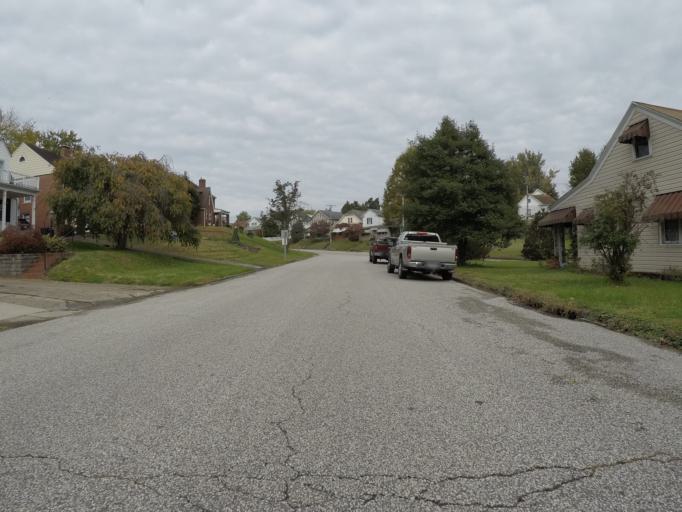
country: US
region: West Virginia
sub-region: Cabell County
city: Huntington
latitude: 38.4075
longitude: -82.4089
